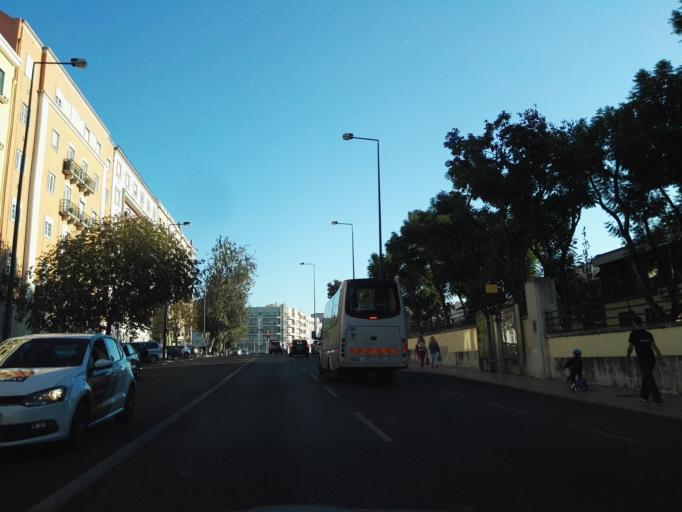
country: PT
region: Lisbon
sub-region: Lisbon
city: Lisbon
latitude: 38.7385
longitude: -9.1368
